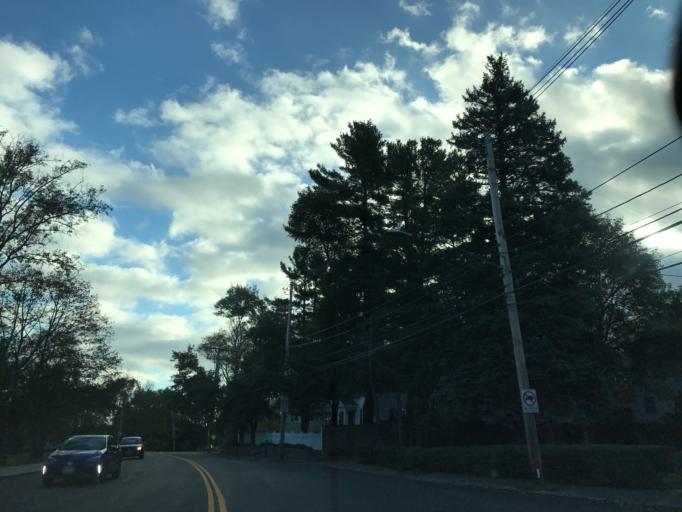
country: US
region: Massachusetts
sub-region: Suffolk County
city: Jamaica Plain
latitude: 42.3092
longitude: -71.1344
